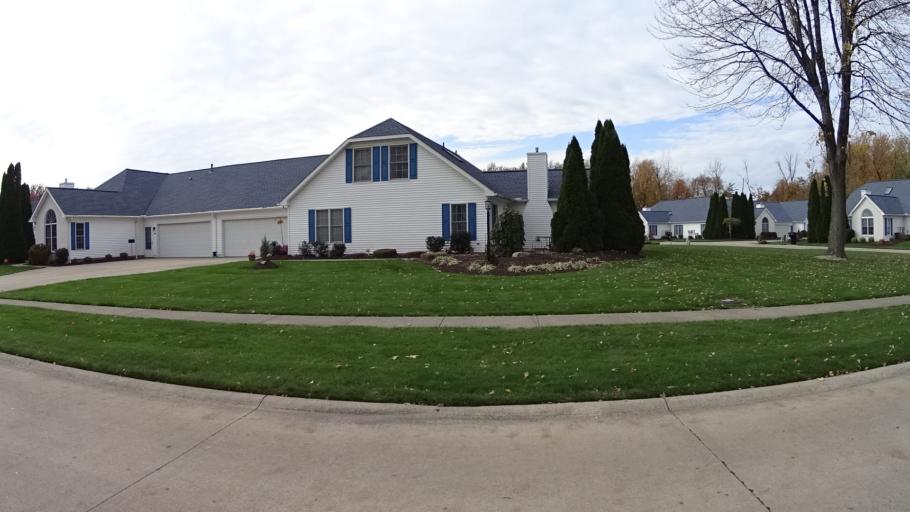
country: US
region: Ohio
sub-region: Lorain County
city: Sheffield Lake
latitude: 41.4826
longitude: -82.1288
